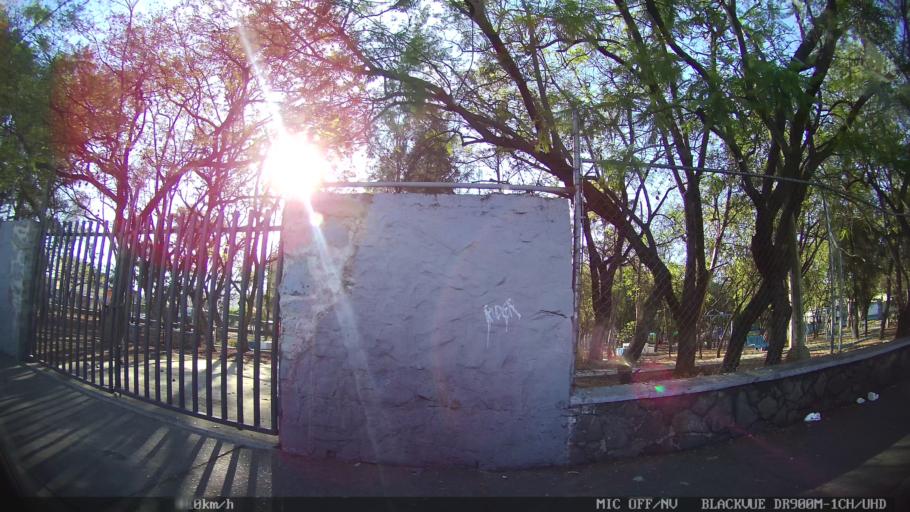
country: MX
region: Jalisco
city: Tlaquepaque
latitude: 20.6543
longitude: -103.2996
